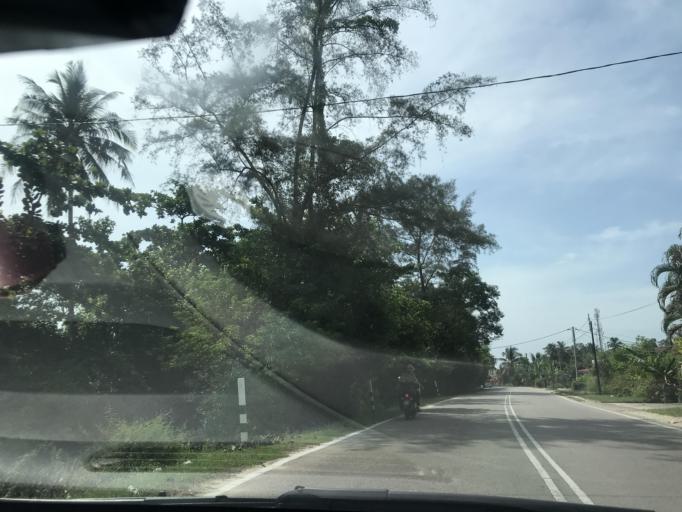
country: MY
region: Kelantan
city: Tumpat
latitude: 6.2163
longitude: 102.1239
